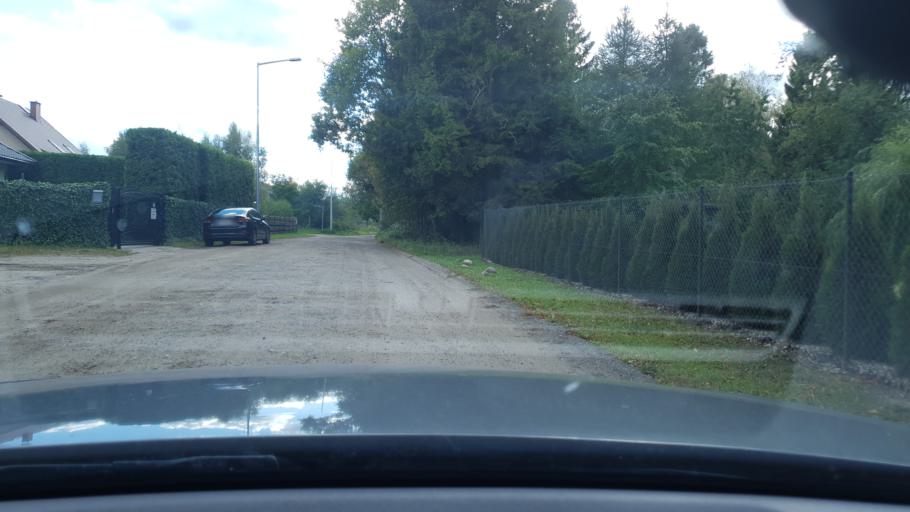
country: PL
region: Pomeranian Voivodeship
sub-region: Powiat wejherowski
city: Reda
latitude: 54.5798
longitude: 18.3122
